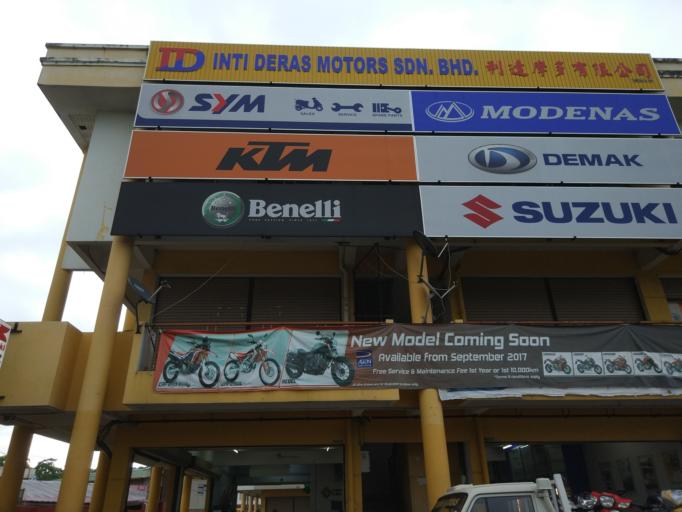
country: MY
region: Sabah
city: Donggongon
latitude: 5.9122
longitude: 116.1002
